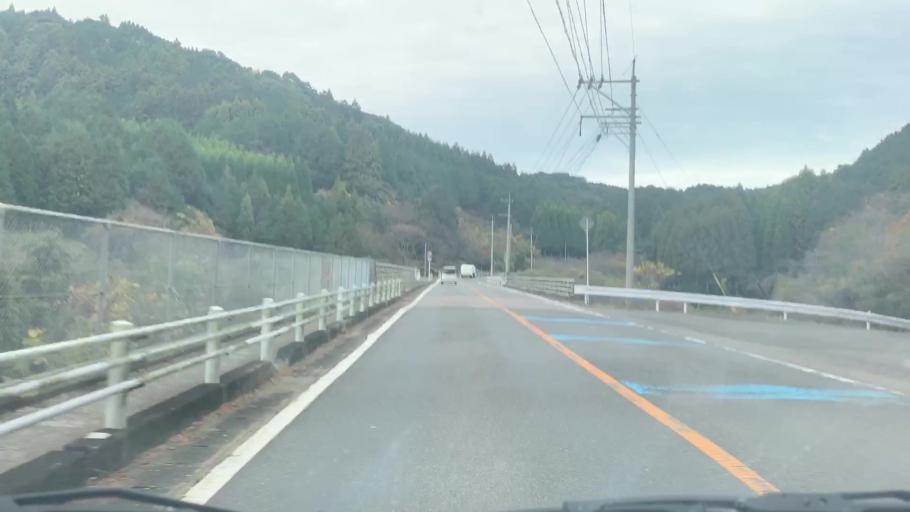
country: JP
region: Saga Prefecture
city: Ureshinomachi-shimojuku
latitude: 33.1594
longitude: 129.9700
